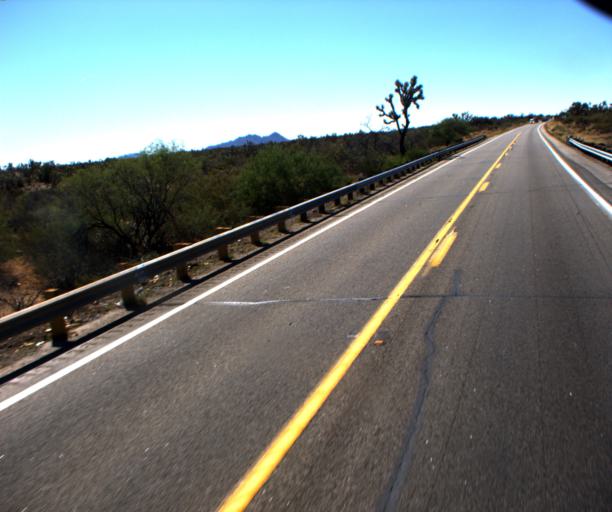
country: US
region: Arizona
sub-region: Yavapai County
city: Congress
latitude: 34.2722
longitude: -113.0957
